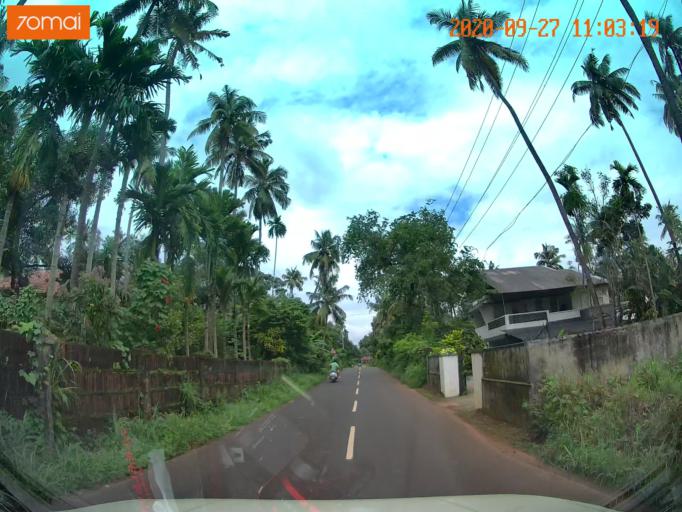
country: IN
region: Kerala
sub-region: Thrissur District
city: Irinjalakuda
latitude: 10.4214
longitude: 76.2581
